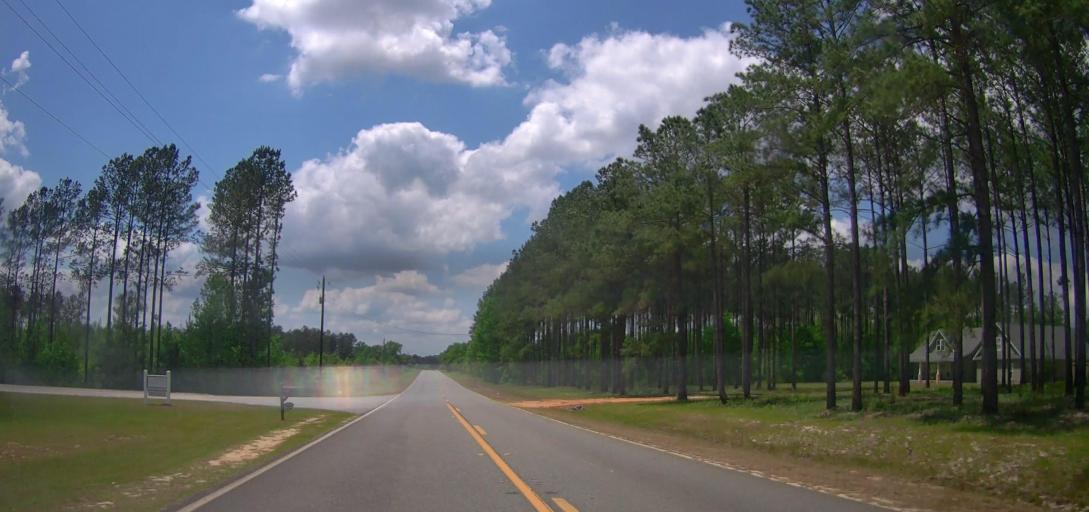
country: US
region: Georgia
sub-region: Laurens County
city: East Dublin
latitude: 32.5282
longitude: -82.7032
